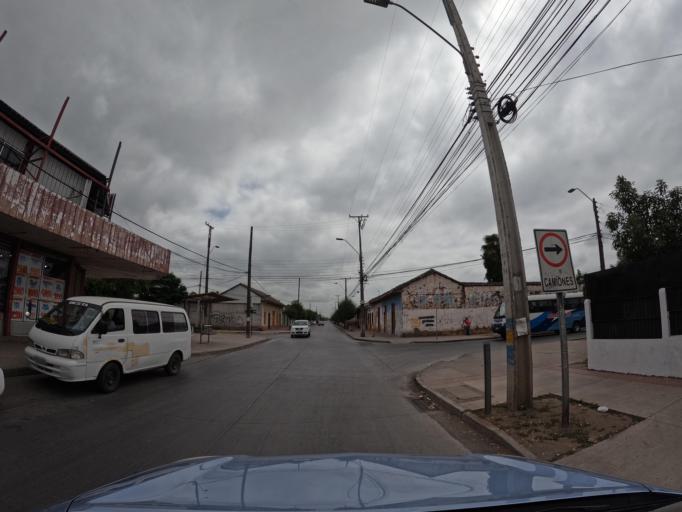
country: CL
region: O'Higgins
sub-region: Provincia de Colchagua
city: Chimbarongo
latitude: -34.7136
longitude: -71.0471
